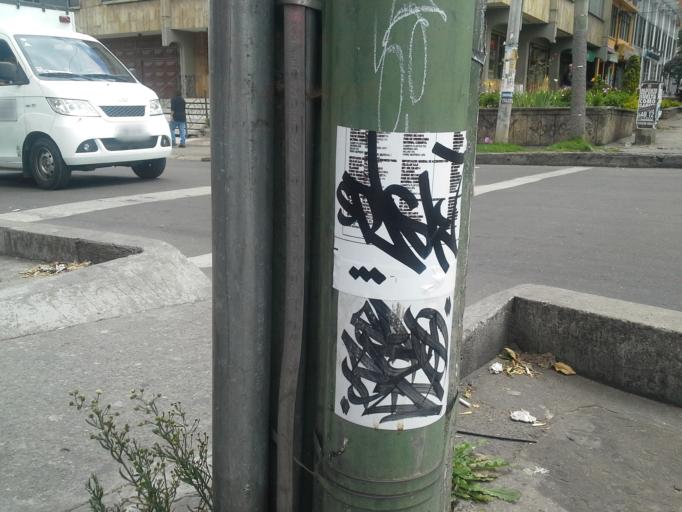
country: CO
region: Bogota D.C.
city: Barrio San Luis
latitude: 4.6621
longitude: -74.0579
